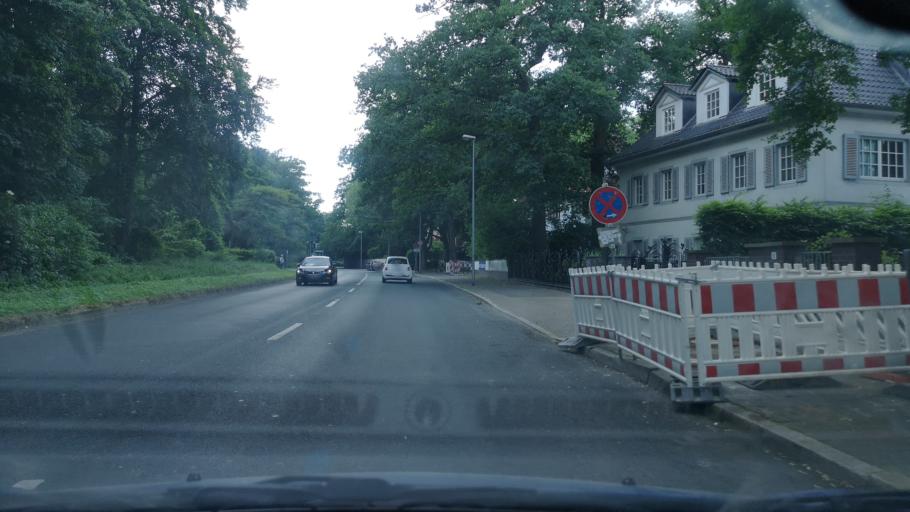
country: DE
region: Lower Saxony
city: Hannover
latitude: 52.3940
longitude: 9.7664
